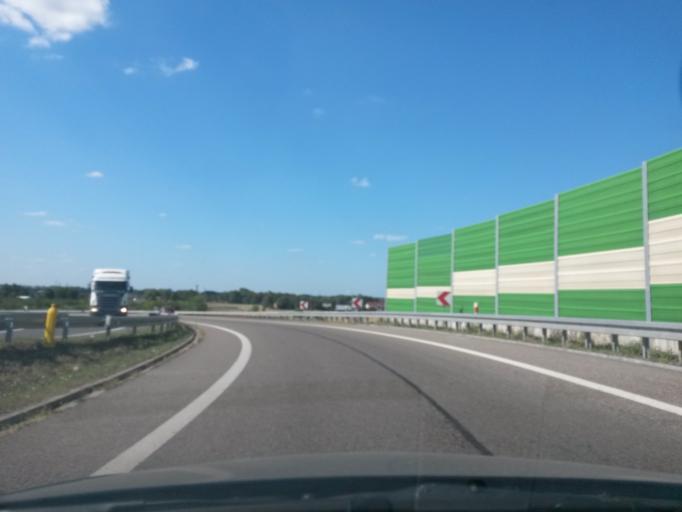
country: PL
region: Masovian Voivodeship
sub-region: Powiat plonski
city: Plonsk
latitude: 52.6050
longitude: 20.4026
